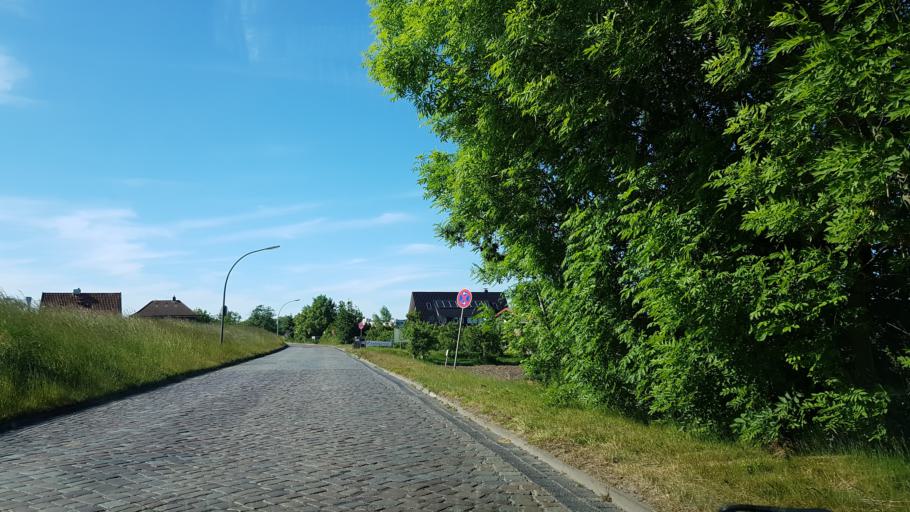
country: DE
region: Lower Saxony
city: Neu Wulmstorf
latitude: 53.5250
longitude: 9.8018
